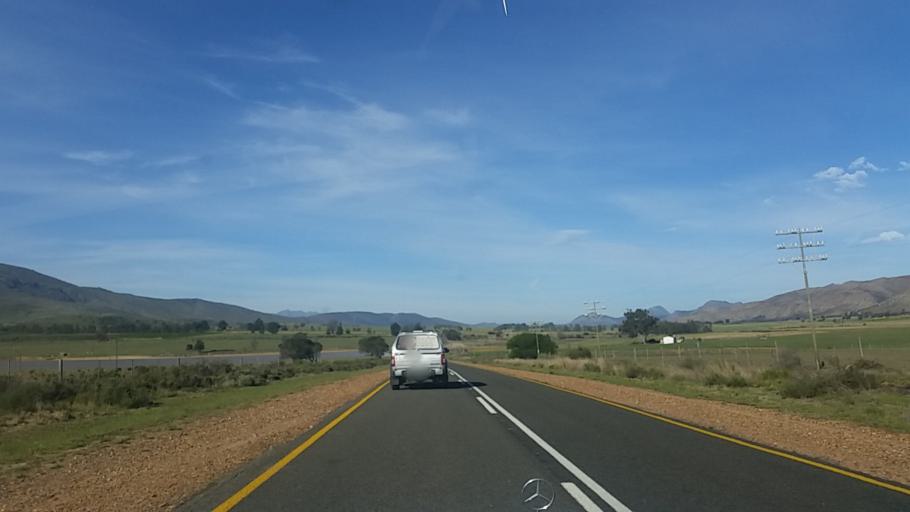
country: ZA
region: Western Cape
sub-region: Eden District Municipality
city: George
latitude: -33.8325
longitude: 22.4552
